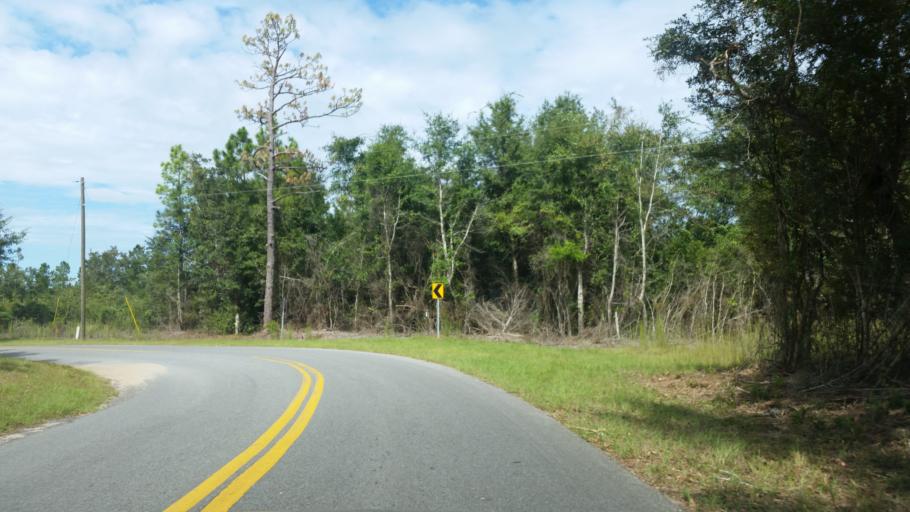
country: US
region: Florida
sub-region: Santa Rosa County
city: Point Baker
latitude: 30.7359
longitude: -87.0134
